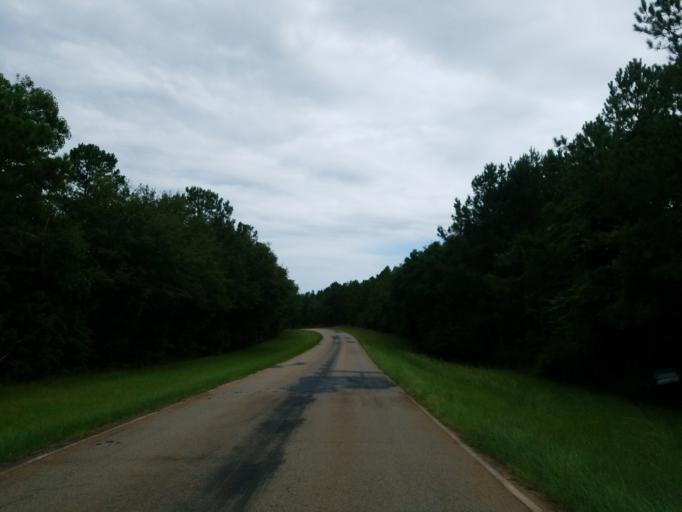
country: US
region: Georgia
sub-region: Monroe County
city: Forsyth
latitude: 32.9609
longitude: -83.9660
